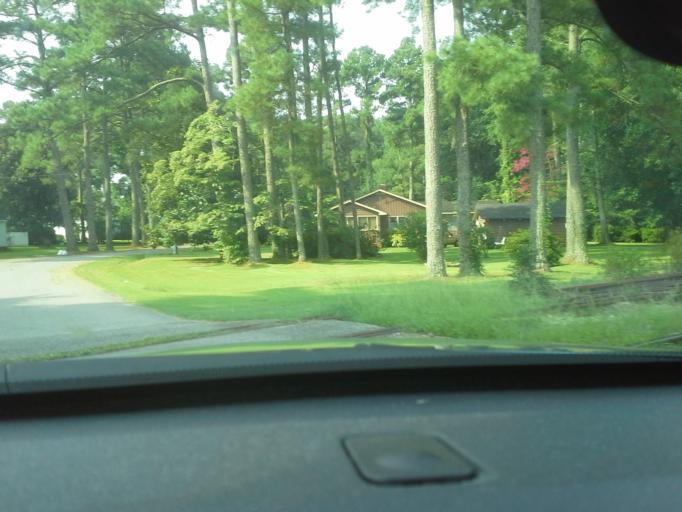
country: US
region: North Carolina
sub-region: Washington County
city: Plymouth
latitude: 35.8620
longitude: -76.7607
